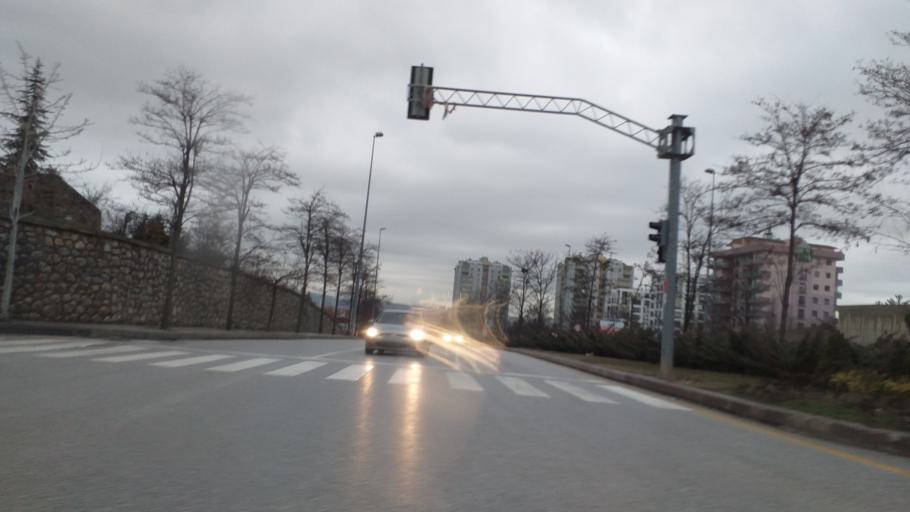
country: TR
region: Ankara
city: Batikent
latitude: 39.8808
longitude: 32.7113
